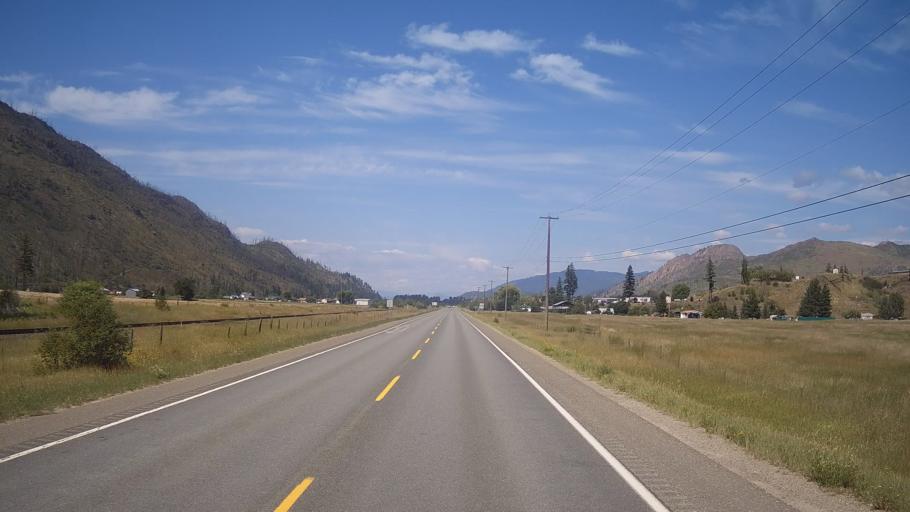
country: CA
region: British Columbia
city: Kamloops
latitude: 51.1273
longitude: -120.1226
